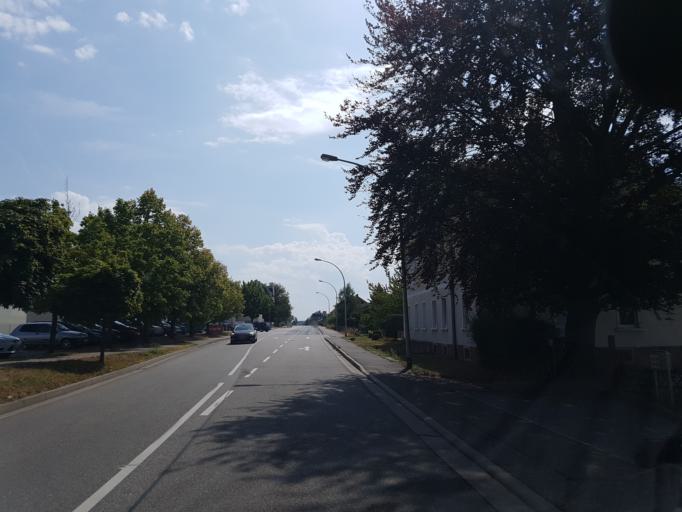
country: DE
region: Saxony
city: Waldheim
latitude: 51.0792
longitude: 13.0009
